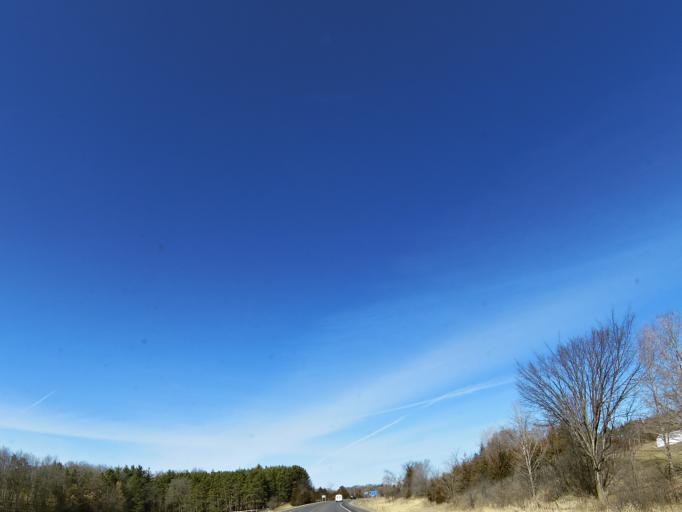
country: US
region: Minnesota
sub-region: Wright County
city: Rockford
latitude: 45.0998
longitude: -93.7731
